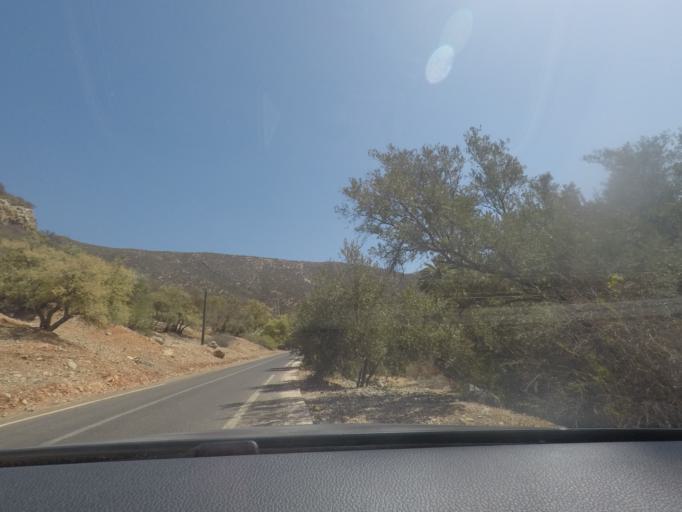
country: MA
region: Souss-Massa-Draa
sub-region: Agadir-Ida-ou-Tnan
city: Aourir
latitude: 30.5977
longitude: -9.5142
